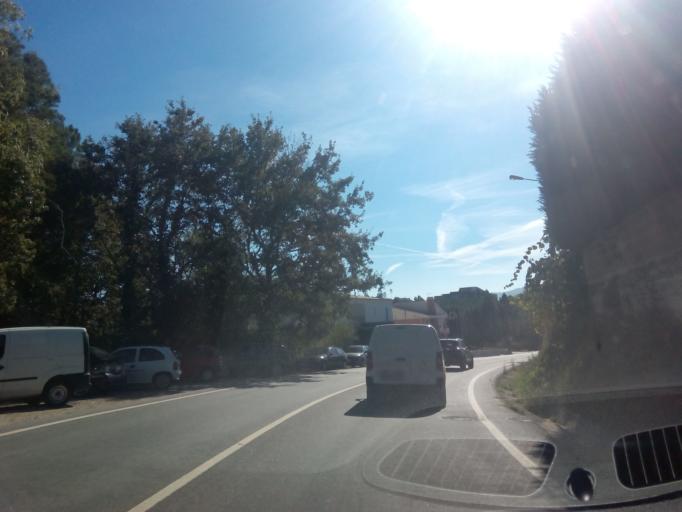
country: PT
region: Porto
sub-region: Paredes
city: Gandra
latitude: 41.1894
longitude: -8.4354
